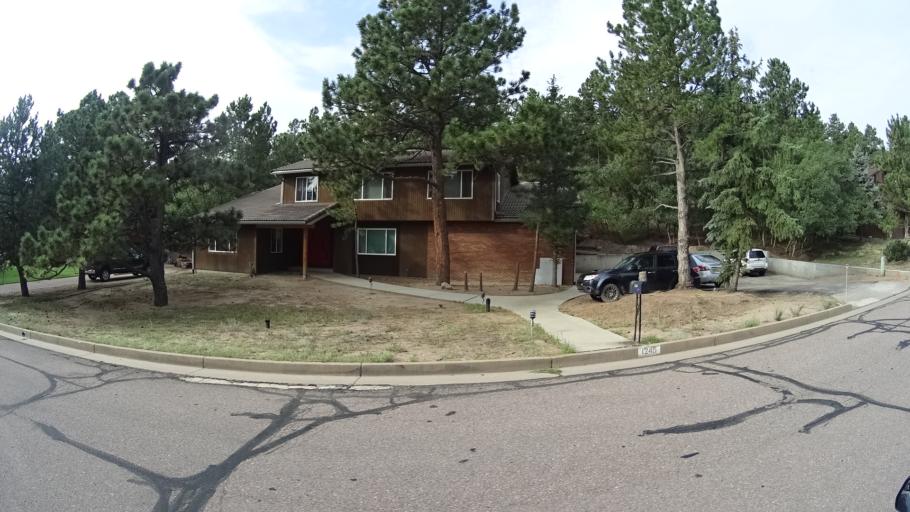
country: US
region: Colorado
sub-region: El Paso County
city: Air Force Academy
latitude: 38.9343
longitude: -104.8514
